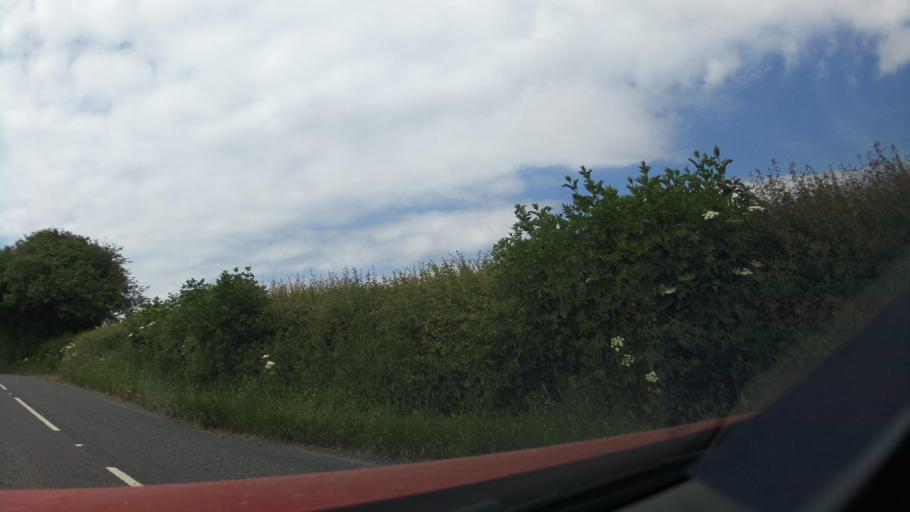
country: GB
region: England
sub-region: Somerset
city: Milborne Port
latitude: 51.0174
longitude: -2.4699
